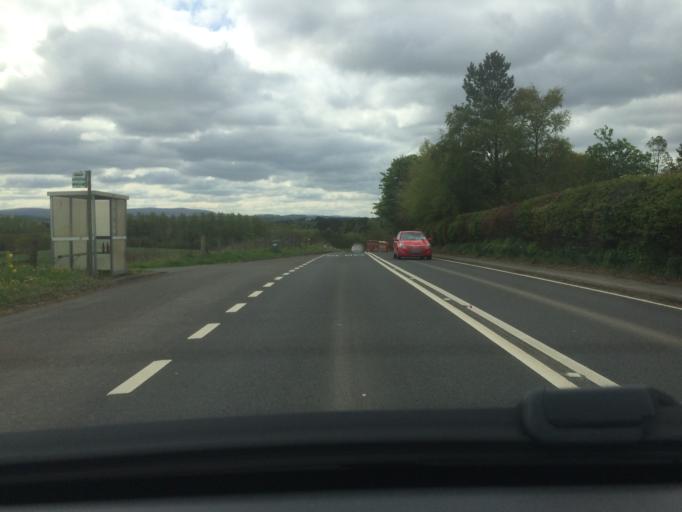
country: GB
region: Scotland
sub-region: Midlothian
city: Penicuik
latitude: 55.8638
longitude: -3.2132
